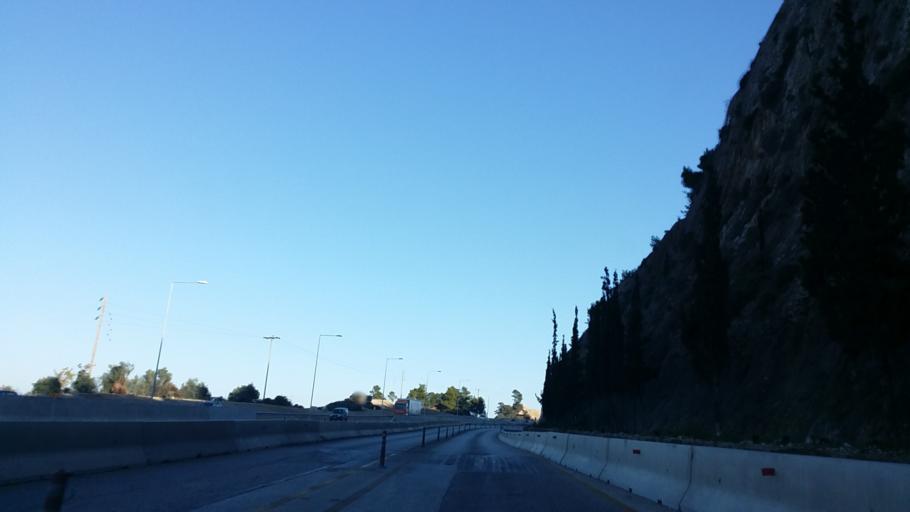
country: GR
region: West Greece
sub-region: Nomos Achaias
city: Akrata
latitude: 38.1742
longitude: 22.2478
